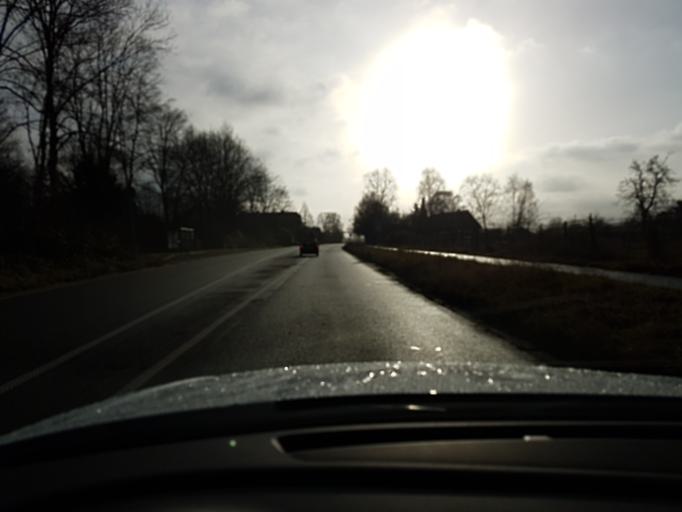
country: DE
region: North Rhine-Westphalia
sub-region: Regierungsbezirk Dusseldorf
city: Muelheim (Ruhr)
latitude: 51.3990
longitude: 6.9007
